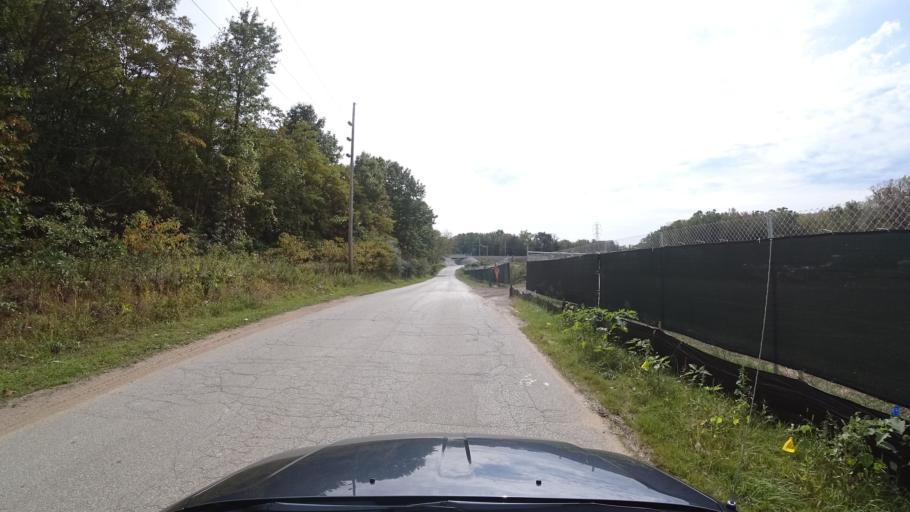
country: US
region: Indiana
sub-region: LaPorte County
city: Trail Creek
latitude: 41.7123
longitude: -86.8553
